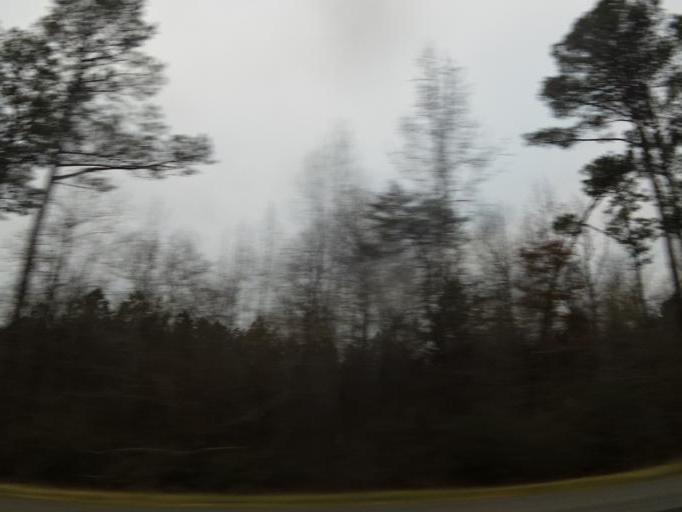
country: US
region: Alabama
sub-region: Blount County
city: Smoke Rise
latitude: 33.9413
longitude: -86.8694
